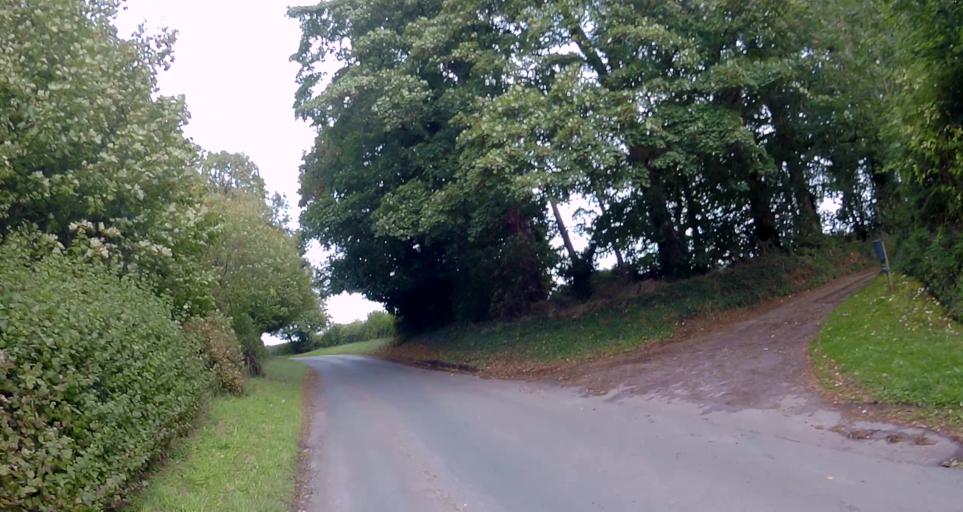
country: GB
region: England
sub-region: Hampshire
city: Four Marks
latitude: 51.0996
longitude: -1.1435
